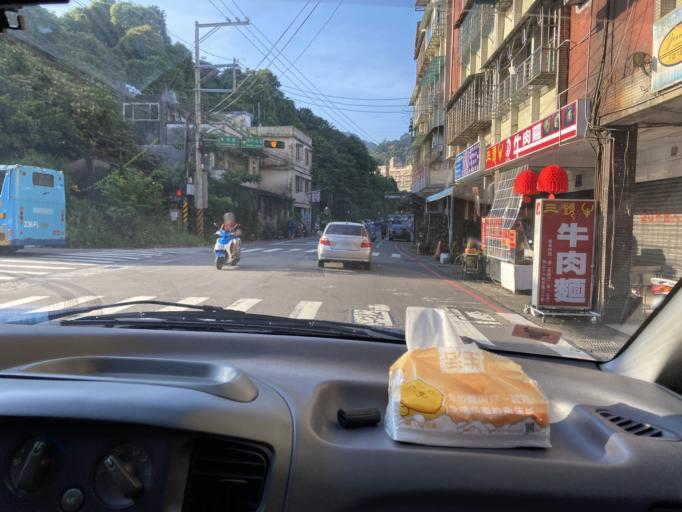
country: TW
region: Taiwan
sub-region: Keelung
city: Keelung
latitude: 25.0947
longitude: 121.7390
